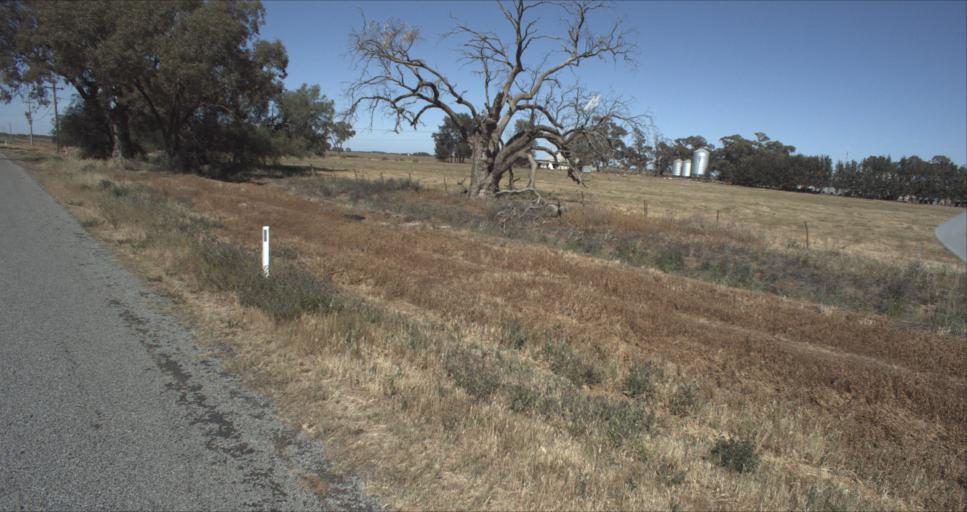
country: AU
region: New South Wales
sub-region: Leeton
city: Leeton
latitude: -34.5428
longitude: 146.3161
